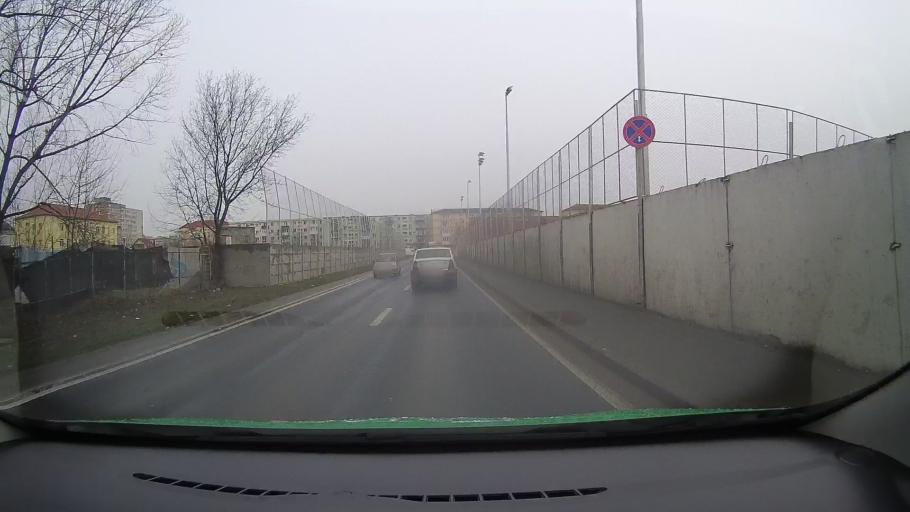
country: RO
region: Timis
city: Timisoara
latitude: 45.7419
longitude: 21.2478
